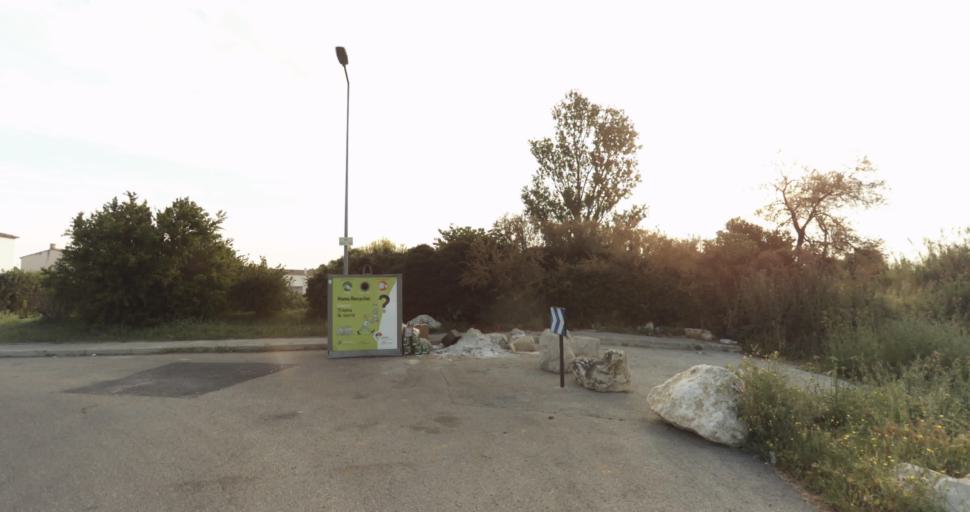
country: FR
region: Languedoc-Roussillon
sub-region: Departement du Gard
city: Caissargues
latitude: 43.8265
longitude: 4.3859
